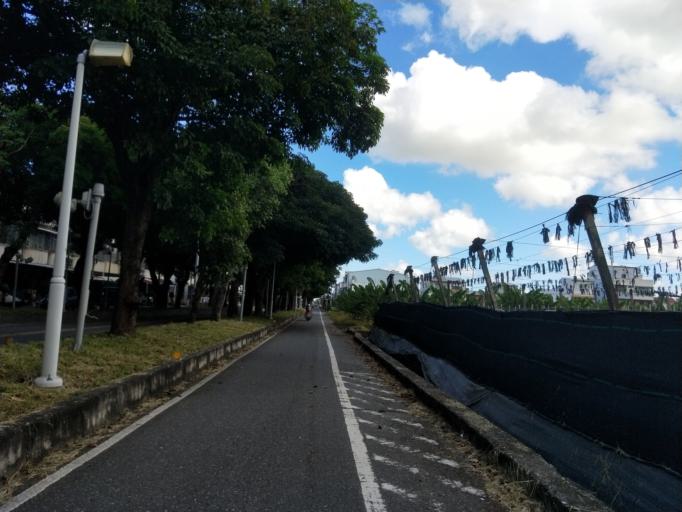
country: TW
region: Taiwan
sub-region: Taitung
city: Taitung
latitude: 22.7912
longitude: 121.1078
